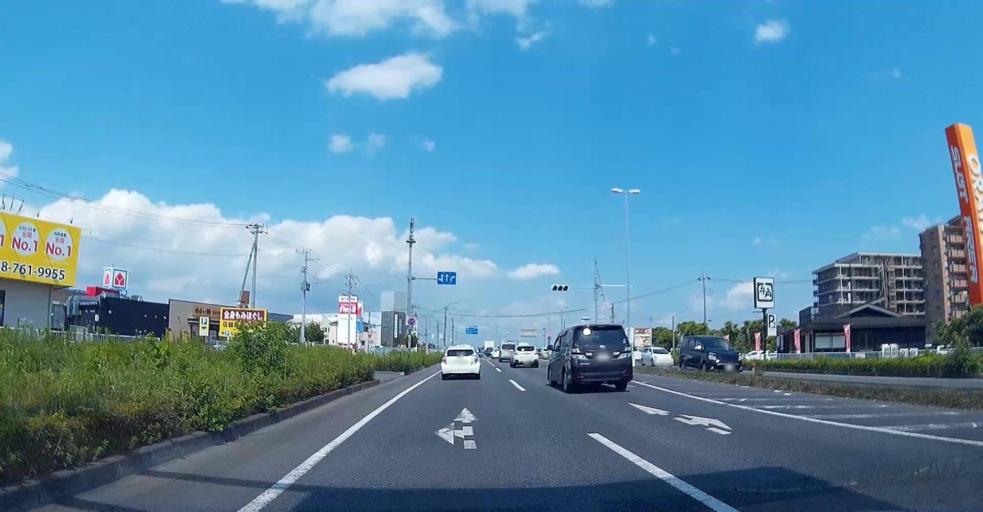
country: JP
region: Saitama
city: Kasukabe
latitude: 35.9927
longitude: 139.7583
